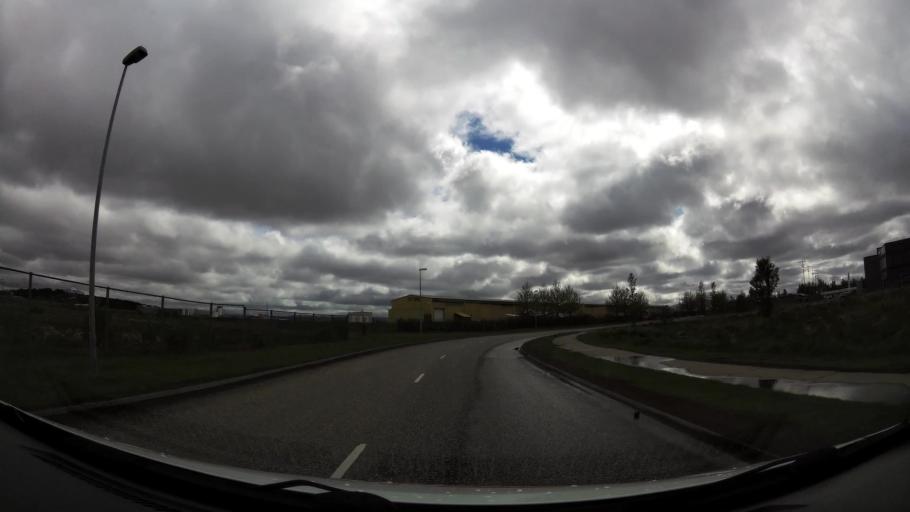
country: IS
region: Capital Region
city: Kopavogur
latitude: 64.1365
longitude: -21.9433
